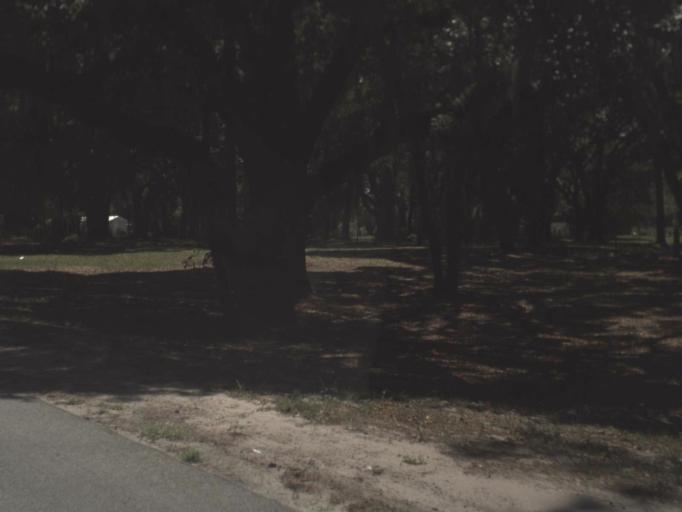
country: US
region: Florida
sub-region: Suwannee County
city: Live Oak
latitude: 30.3321
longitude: -83.0653
